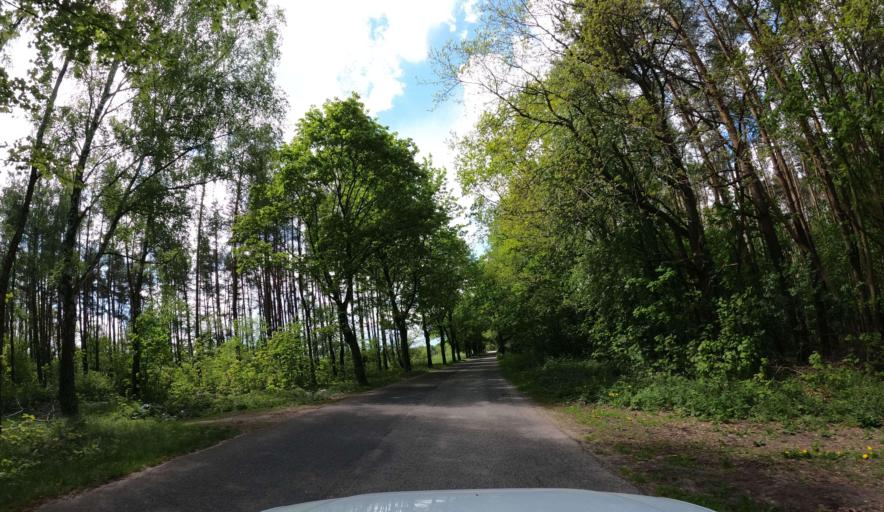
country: PL
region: West Pomeranian Voivodeship
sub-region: Powiat kamienski
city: Wolin
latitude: 53.8786
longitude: 14.6527
